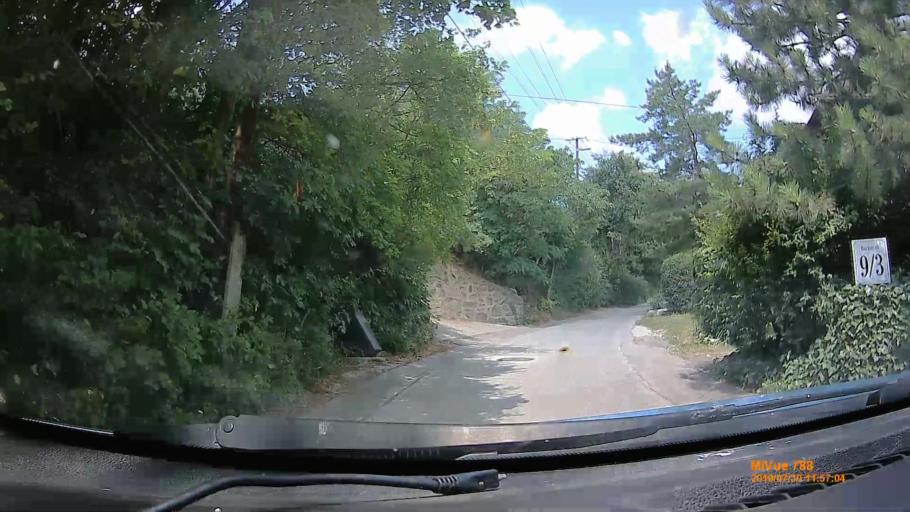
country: HU
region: Baranya
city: Pecs
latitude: 46.0858
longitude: 18.2180
